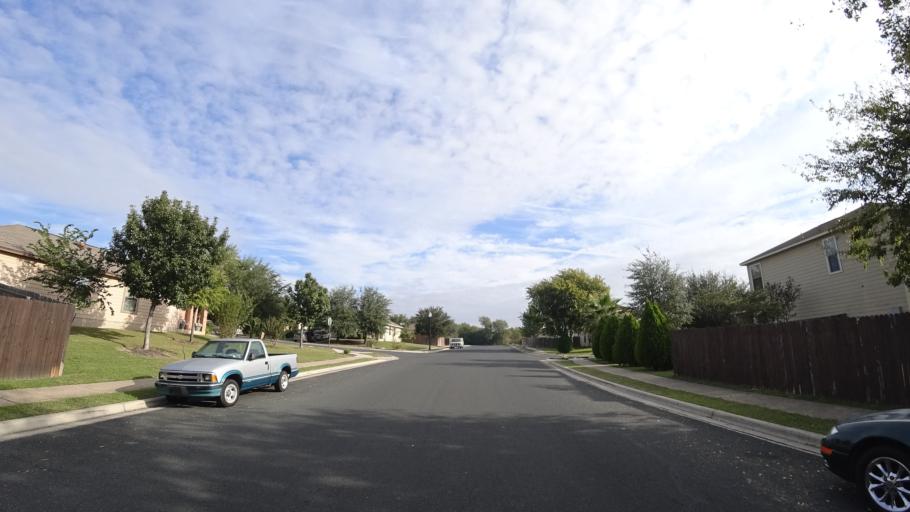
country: US
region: Texas
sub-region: Travis County
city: Austin
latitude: 30.1989
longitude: -97.7296
